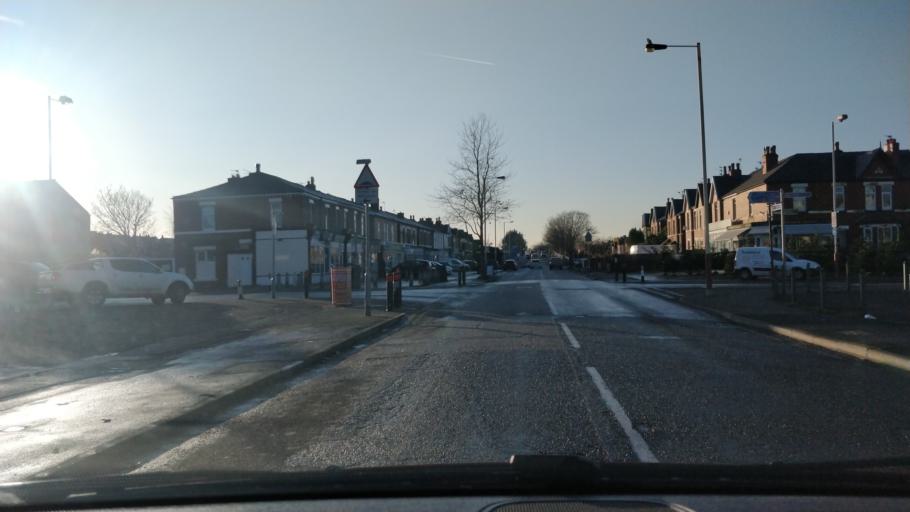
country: GB
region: England
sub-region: Sefton
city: Southport
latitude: 53.6476
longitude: -2.9713
